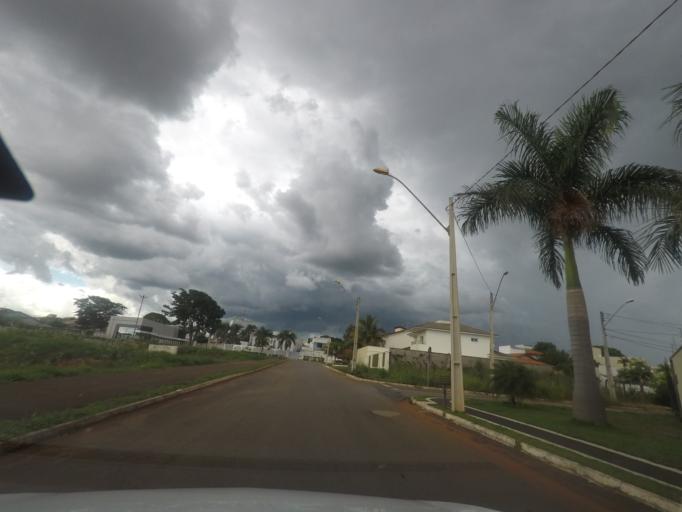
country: BR
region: Goias
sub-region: Goiania
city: Goiania
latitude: -16.6422
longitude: -49.2281
